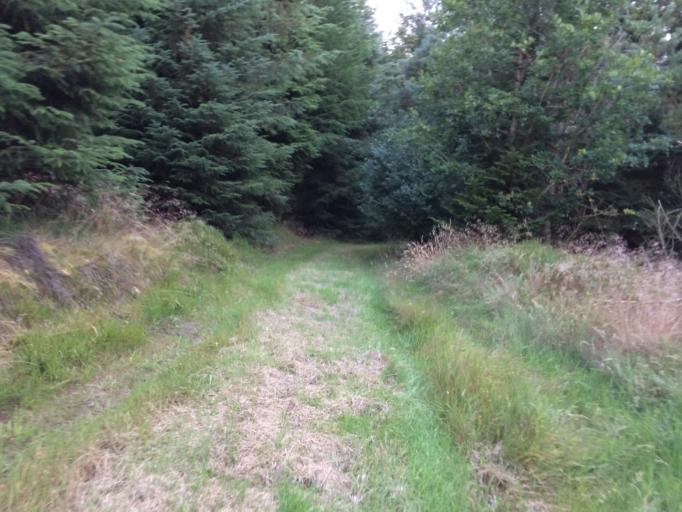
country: DK
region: Central Jutland
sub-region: Holstebro Kommune
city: Ulfborg
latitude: 56.2530
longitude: 8.3719
